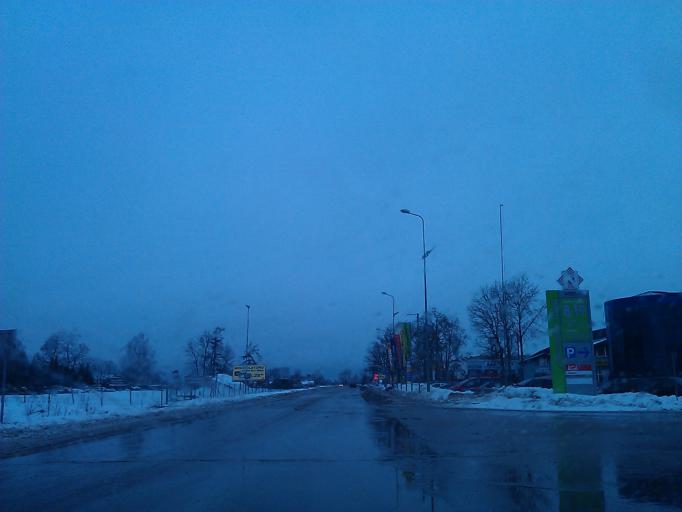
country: LV
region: Cesu Rajons
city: Cesis
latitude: 57.2958
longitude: 25.3031
